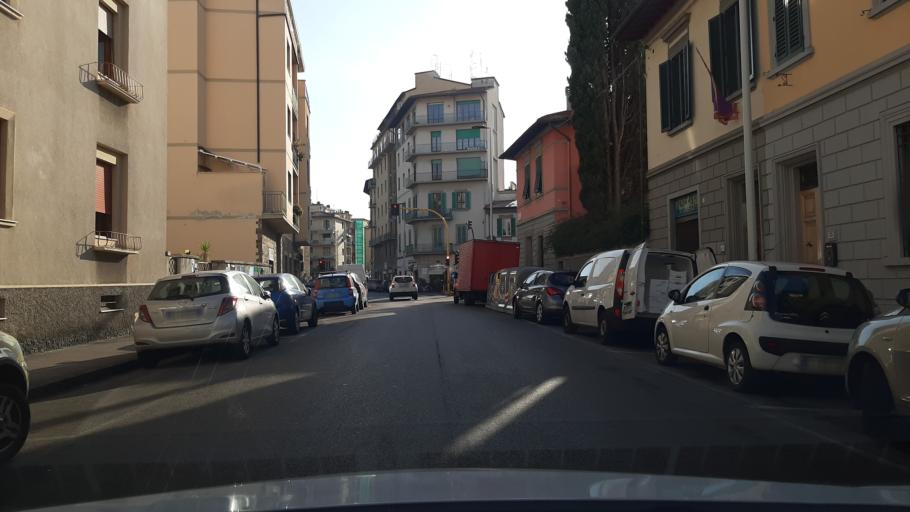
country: IT
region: Tuscany
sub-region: Province of Florence
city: Fiesole
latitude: 43.7828
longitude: 11.2863
